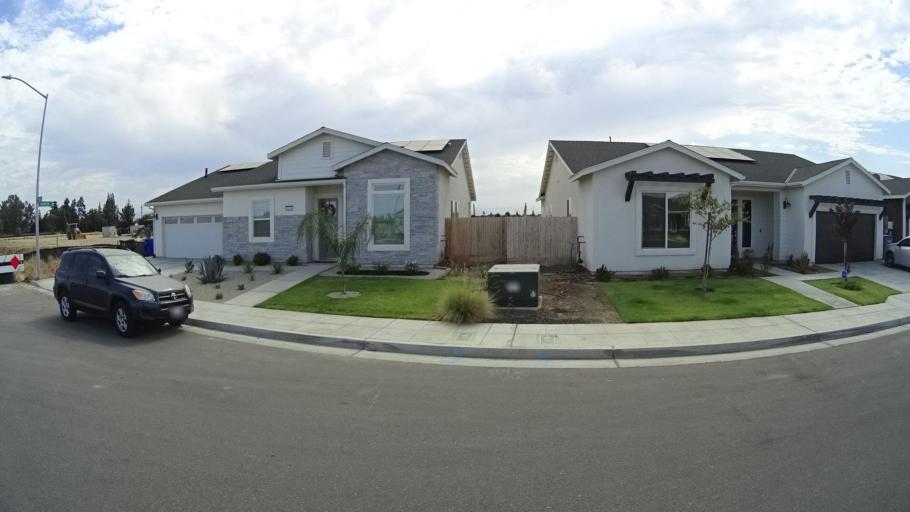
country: US
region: California
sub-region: Fresno County
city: Tarpey Village
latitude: 36.7850
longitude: -119.6769
